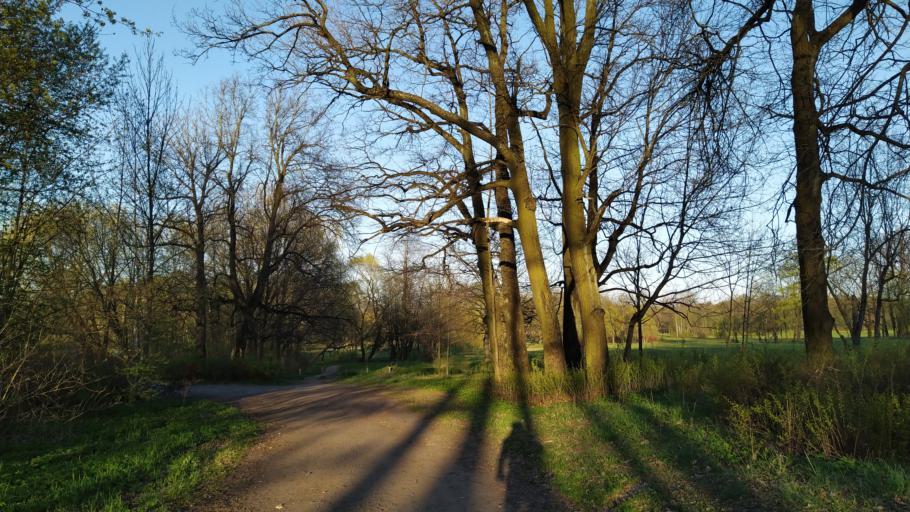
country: RU
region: St.-Petersburg
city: Pushkin
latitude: 59.7114
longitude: 30.4174
